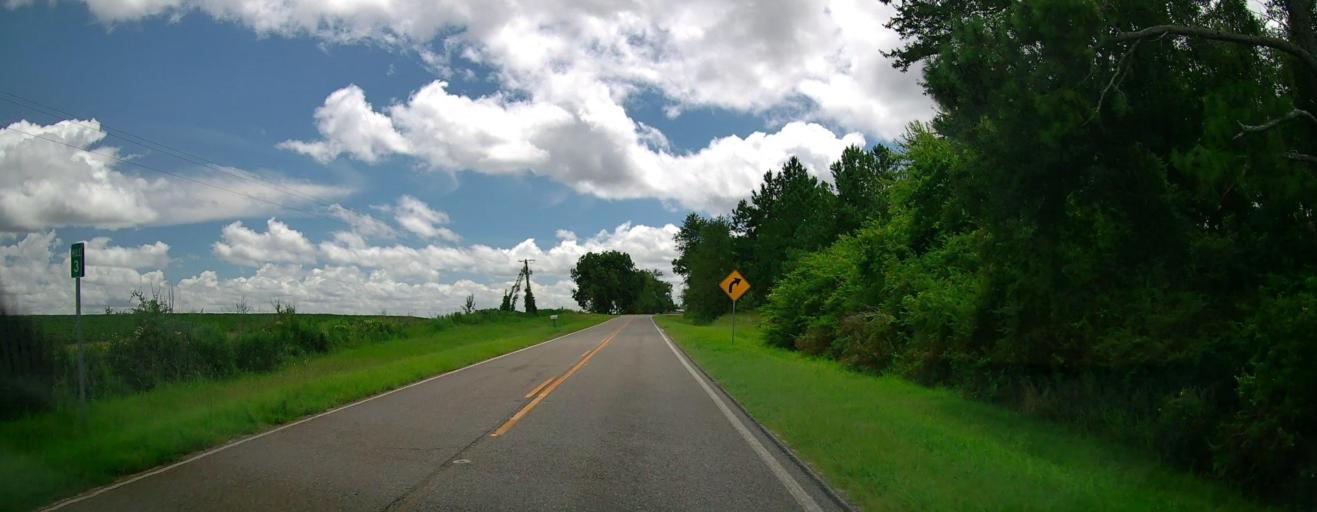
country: US
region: Georgia
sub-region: Wilcox County
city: Rochelle
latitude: 31.8974
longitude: -83.5530
